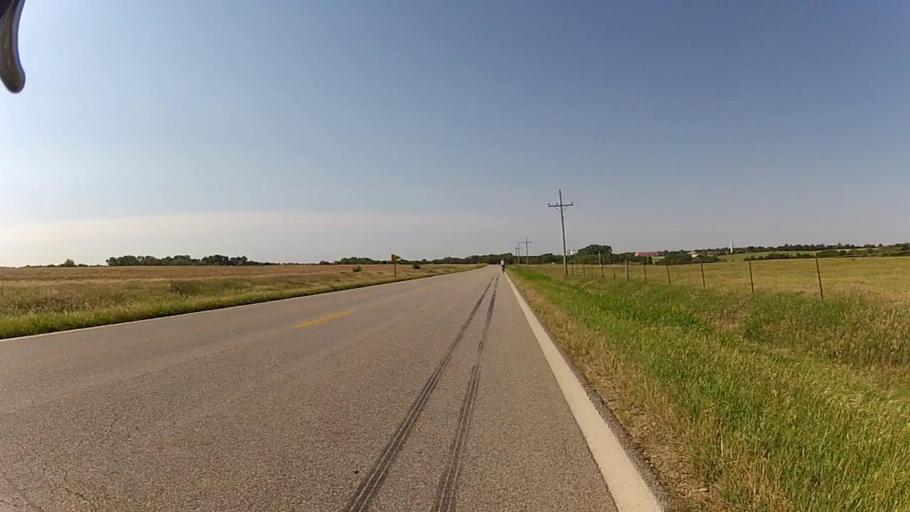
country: US
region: Kansas
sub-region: Sumner County
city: Caldwell
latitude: 37.0499
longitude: -97.6007
